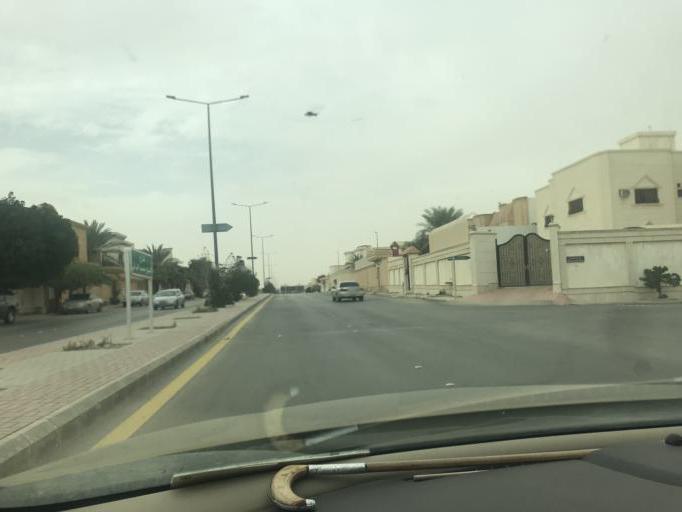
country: SA
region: Ar Riyad
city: Riyadh
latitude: 24.7384
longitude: 46.7541
